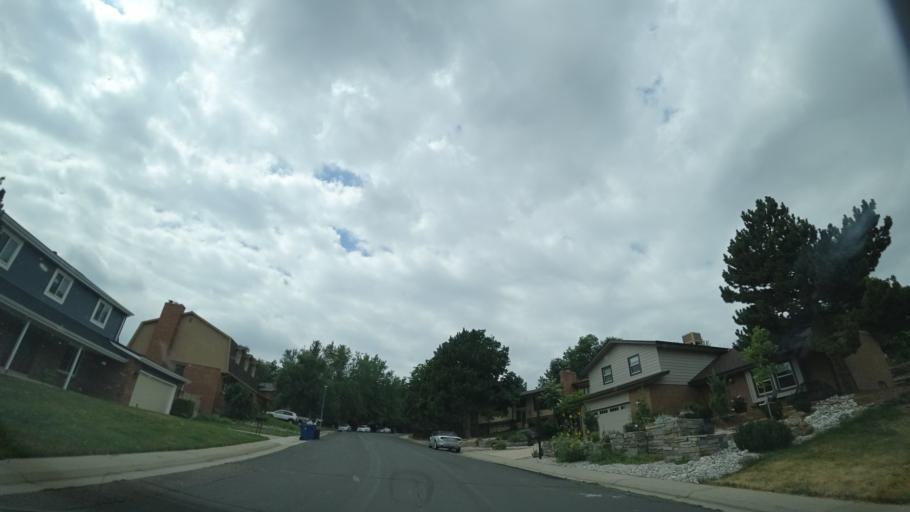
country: US
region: Colorado
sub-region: Jefferson County
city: West Pleasant View
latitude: 39.7206
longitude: -105.1632
